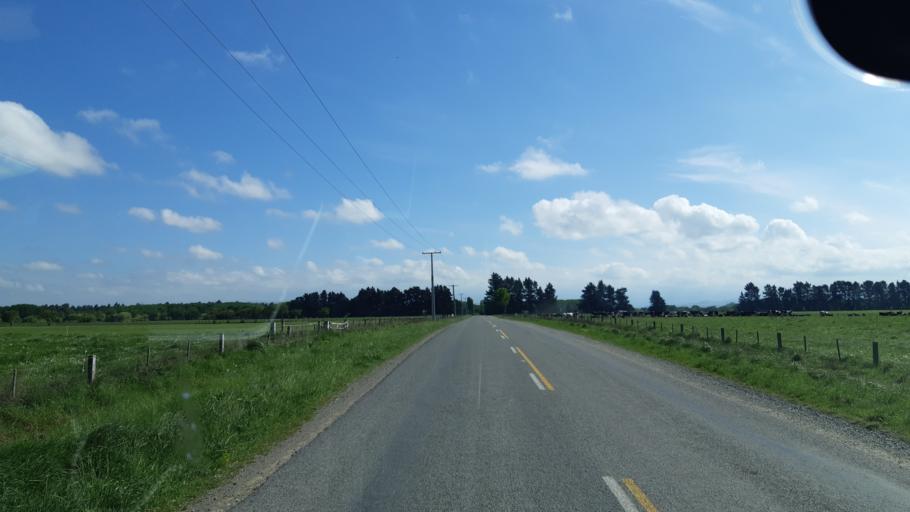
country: NZ
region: Canterbury
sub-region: Timaru District
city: Pleasant Point
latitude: -44.2430
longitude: 171.1560
